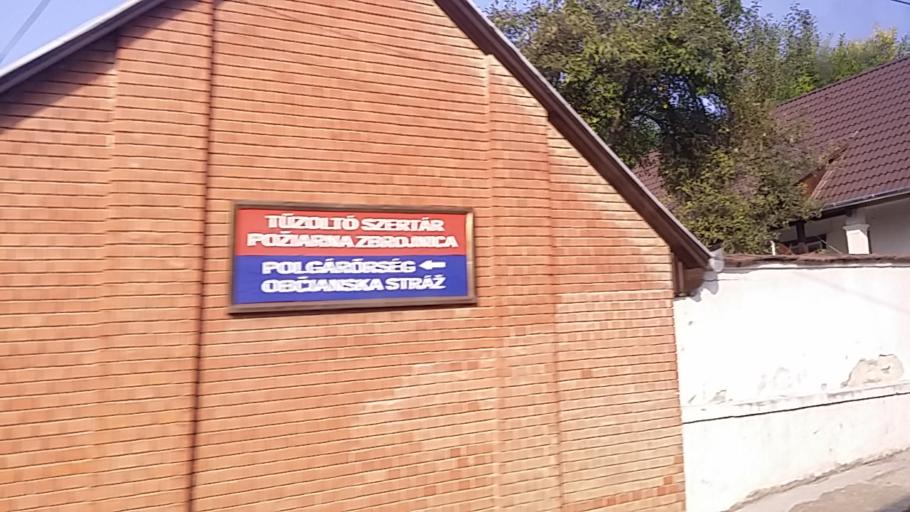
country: HU
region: Pest
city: Pilisszanto
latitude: 47.6709
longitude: 18.8867
